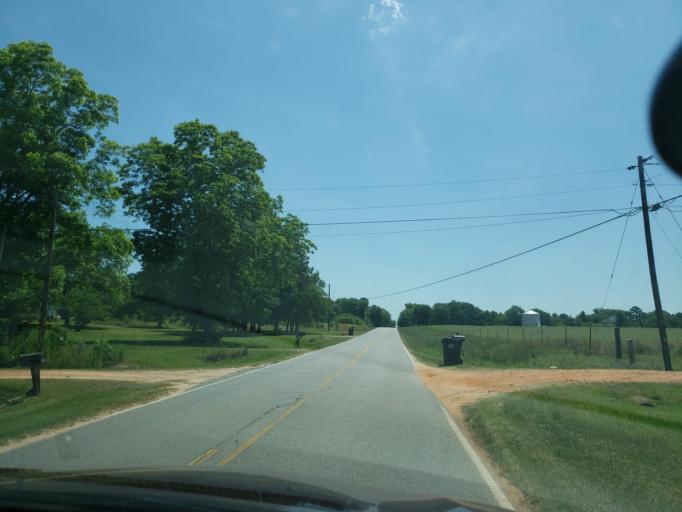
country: US
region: Alabama
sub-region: Elmore County
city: Tallassee
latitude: 32.5811
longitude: -85.7946
